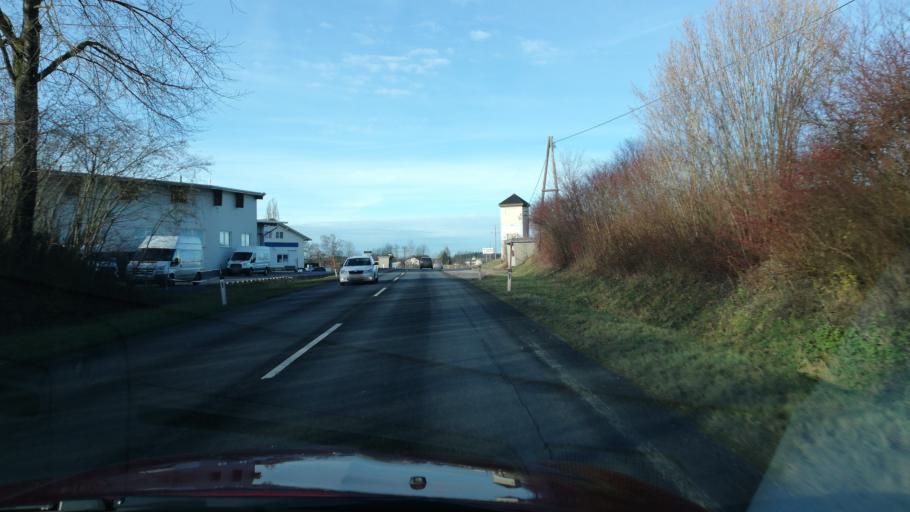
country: AT
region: Upper Austria
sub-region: Wels-Land
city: Sattledt
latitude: 48.0515
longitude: 14.0572
